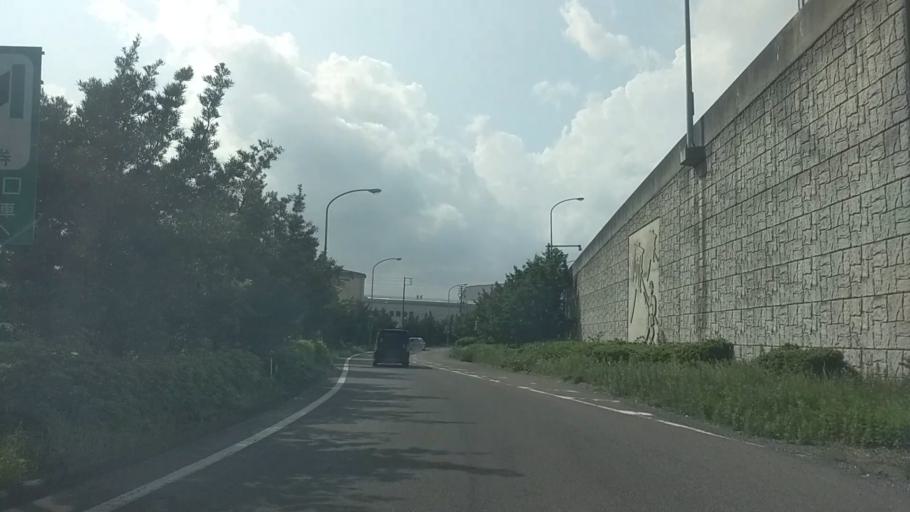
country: JP
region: Shizuoka
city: Hamakita
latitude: 34.7429
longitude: 137.7900
